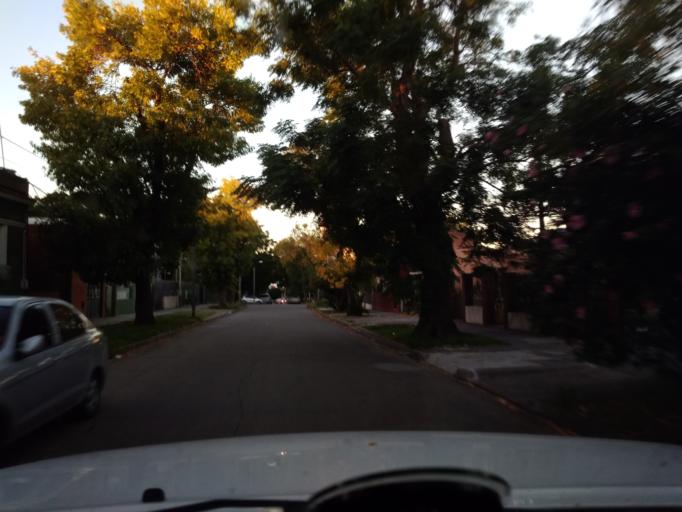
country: UY
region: Montevideo
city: Montevideo
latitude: -34.8954
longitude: -56.1246
